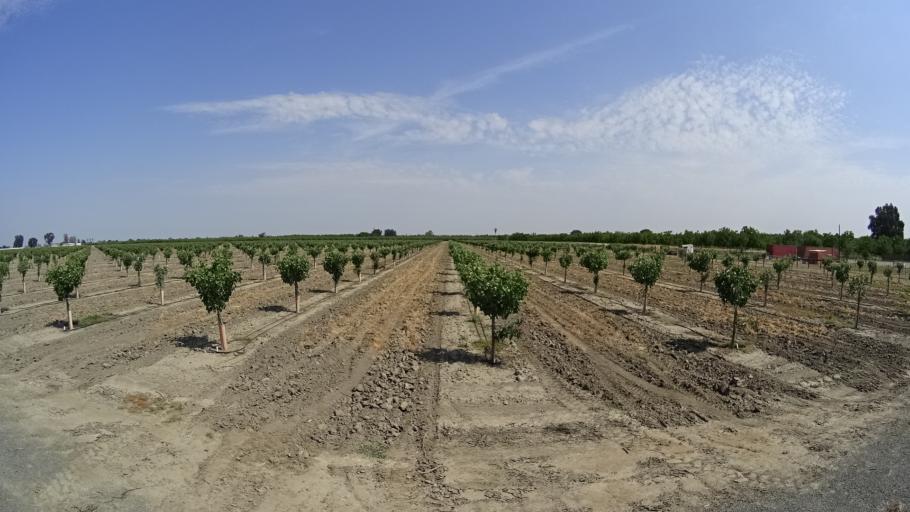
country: US
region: California
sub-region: Fresno County
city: Riverdale
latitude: 36.3948
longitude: -119.7739
